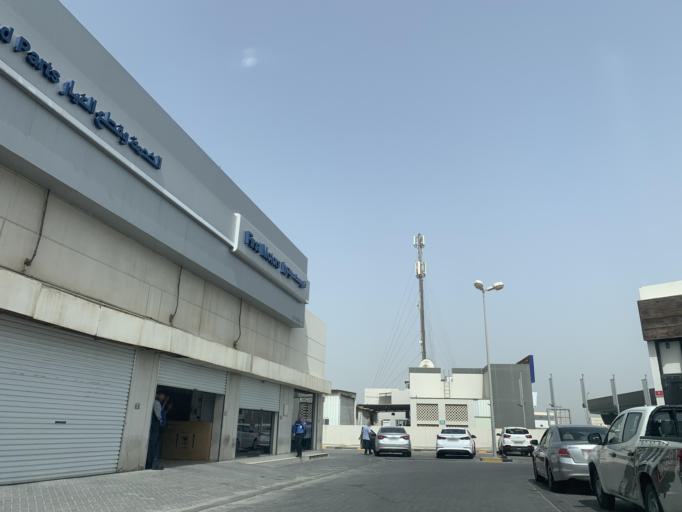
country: BH
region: Northern
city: Madinat `Isa
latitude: 26.1871
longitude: 50.5176
